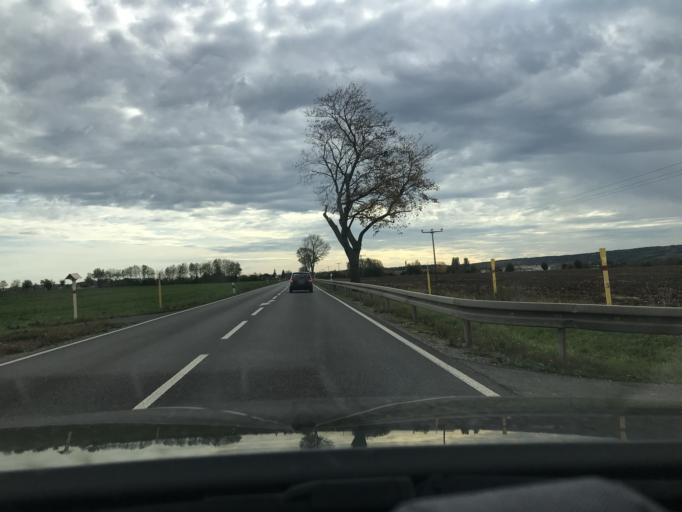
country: DE
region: Thuringia
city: Warza
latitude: 51.0075
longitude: 10.6855
